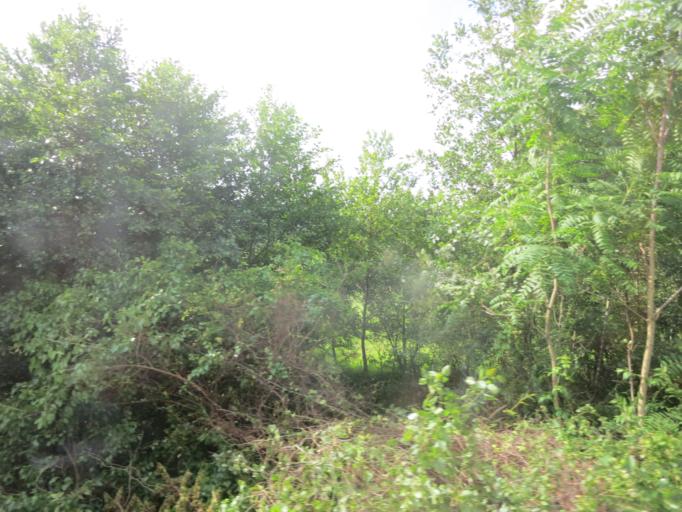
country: GE
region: Guria
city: Lanchkhuti
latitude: 42.0842
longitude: 41.9450
